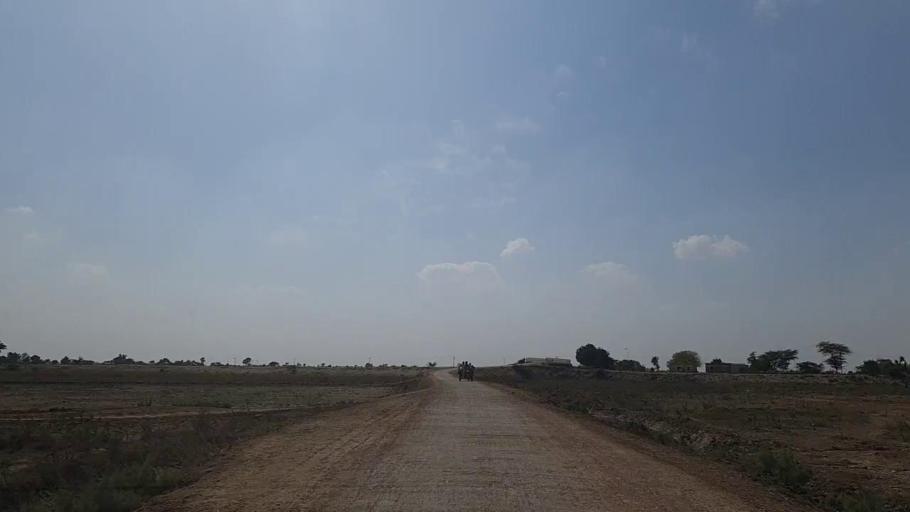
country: PK
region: Sindh
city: Jati
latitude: 24.4788
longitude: 68.2708
